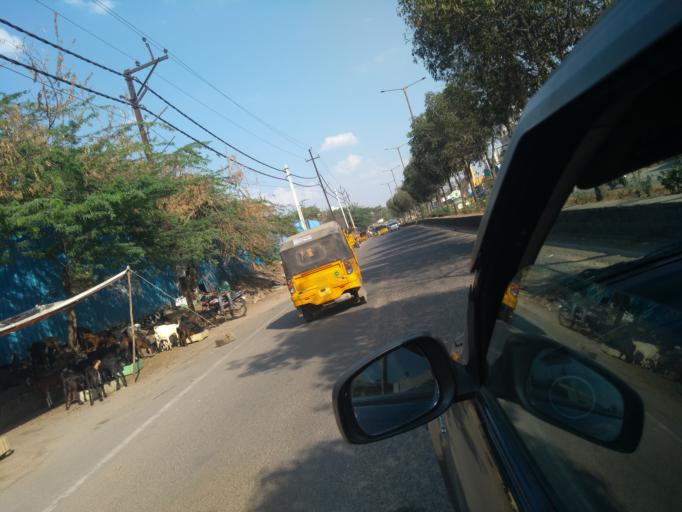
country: IN
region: Telangana
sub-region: Hyderabad
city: Hyderabad
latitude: 17.3760
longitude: 78.4350
